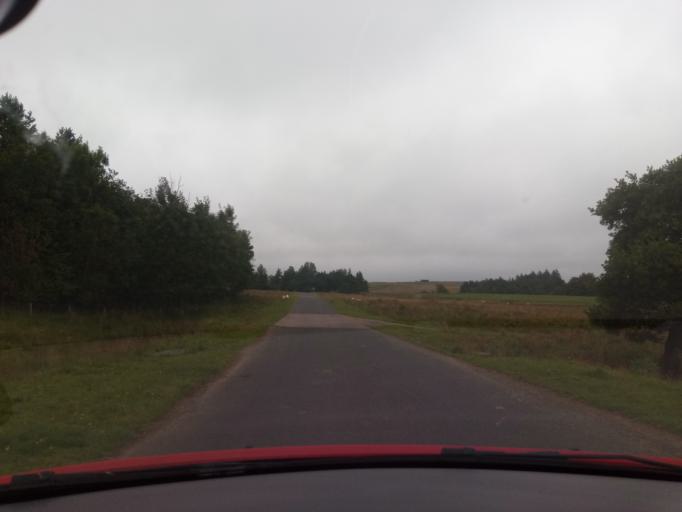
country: GB
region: England
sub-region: Northumberland
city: Otterburn
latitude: 55.2724
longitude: -2.1058
